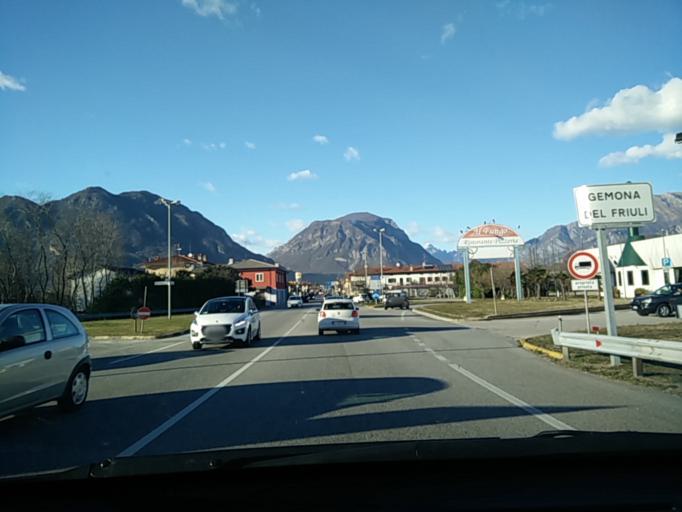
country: IT
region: Friuli Venezia Giulia
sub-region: Provincia di Udine
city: Gemona
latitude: 46.2617
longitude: 13.1083
